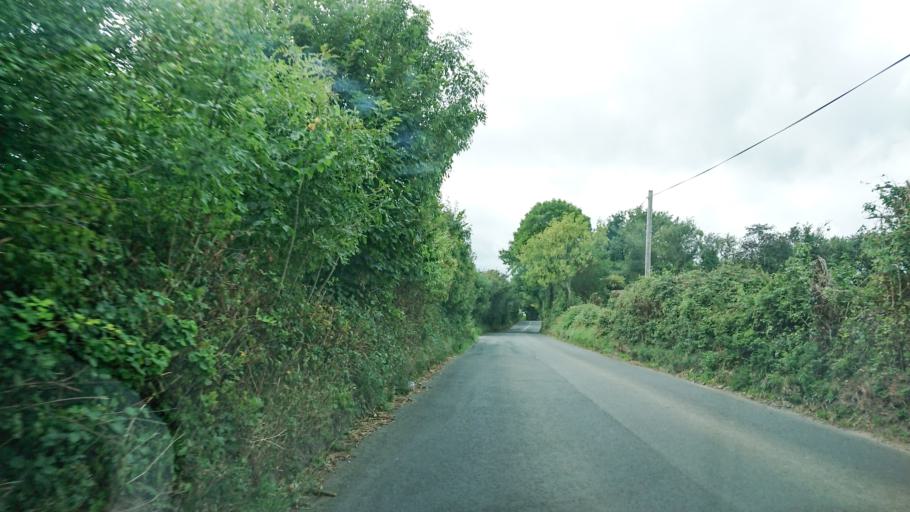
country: IE
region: Munster
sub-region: County Cork
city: Mallow
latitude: 52.1527
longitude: -8.5489
